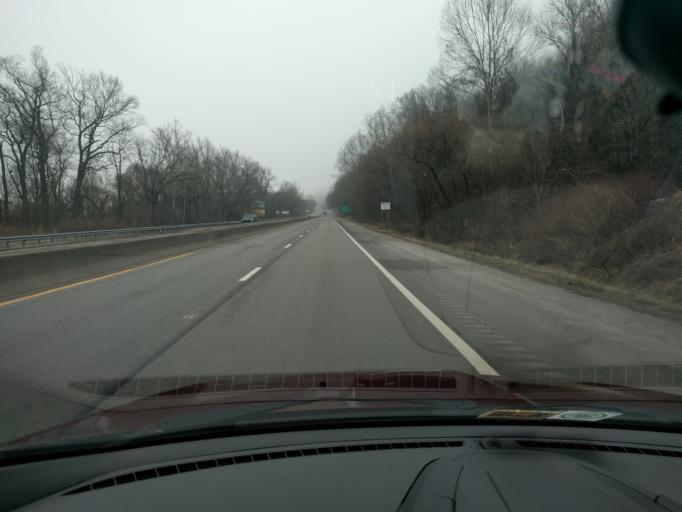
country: US
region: West Virginia
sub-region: Kanawha County
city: Rand
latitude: 38.2901
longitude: -81.5598
